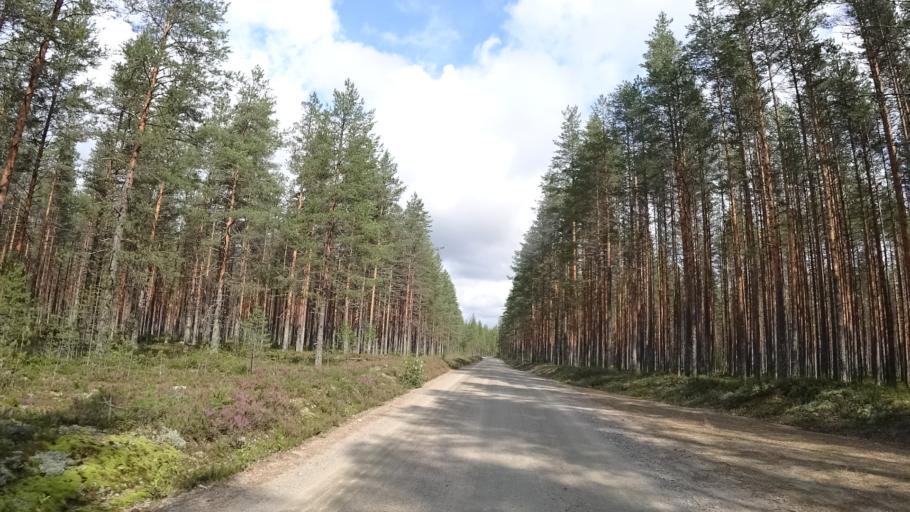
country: FI
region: North Karelia
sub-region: Joensuu
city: Ilomantsi
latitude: 62.9353
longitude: 31.4303
